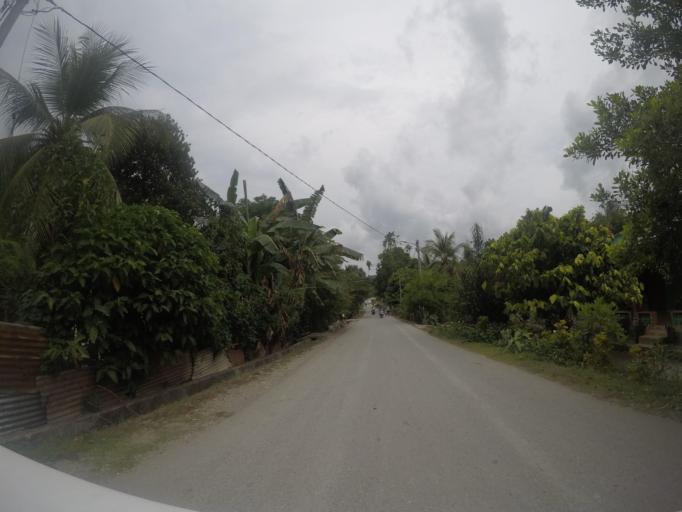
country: TL
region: Viqueque
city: Viqueque
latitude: -8.8707
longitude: 126.3638
